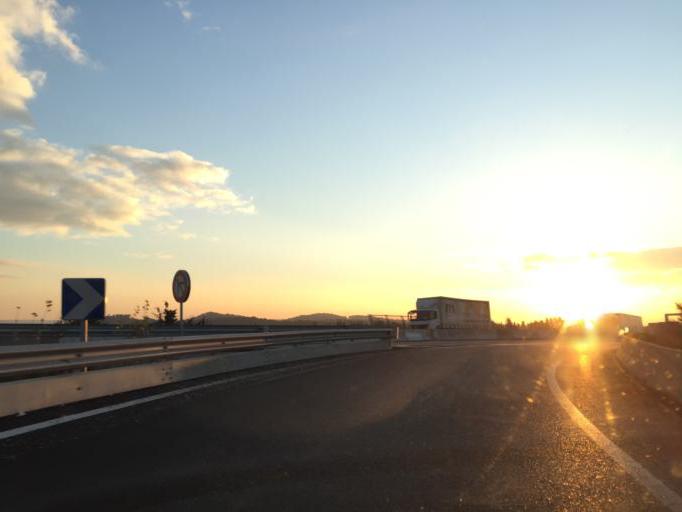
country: FR
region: Provence-Alpes-Cote d'Azur
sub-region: Departement du Vaucluse
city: Cavaillon
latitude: 43.8233
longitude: 5.0287
